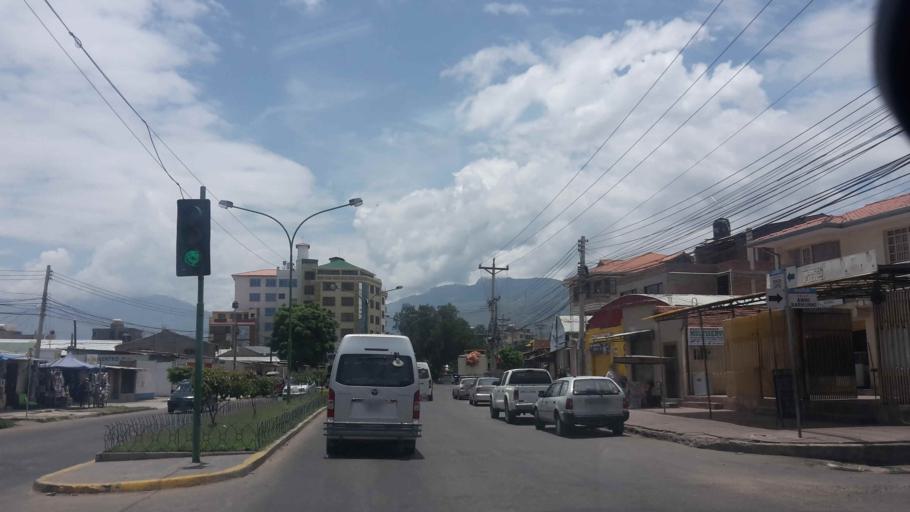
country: BO
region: Cochabamba
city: Cochabamba
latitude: -17.3625
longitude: -66.1803
